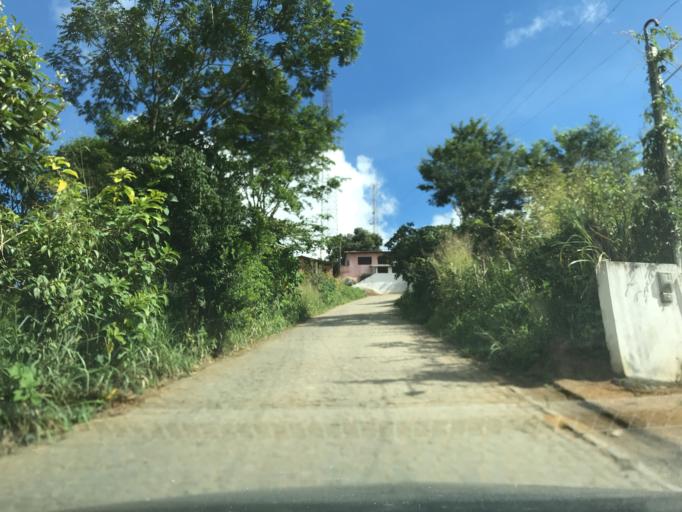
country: BR
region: Pernambuco
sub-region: Bezerros
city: Bezerros
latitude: -8.1639
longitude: -35.7669
